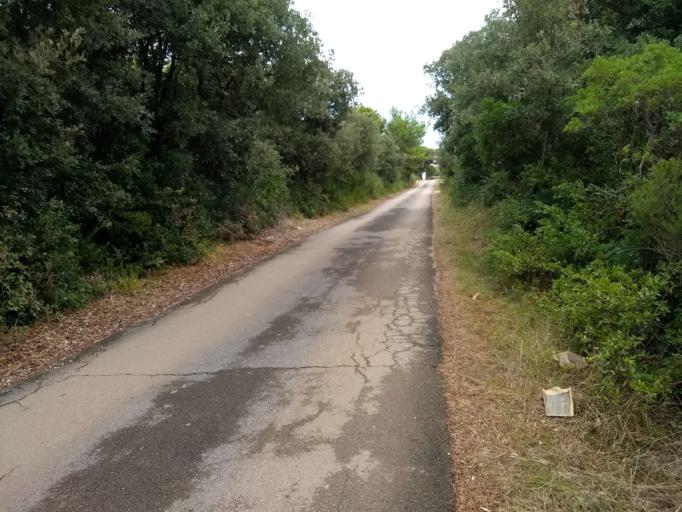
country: HR
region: Zadarska
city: Ugljan
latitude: 44.1422
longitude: 15.0817
